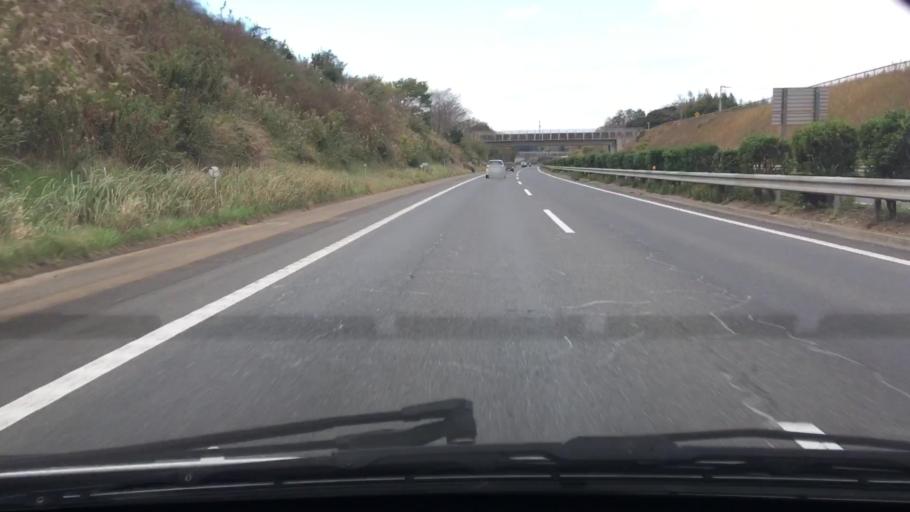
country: JP
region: Chiba
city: Ichihara
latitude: 35.4247
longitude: 140.0307
